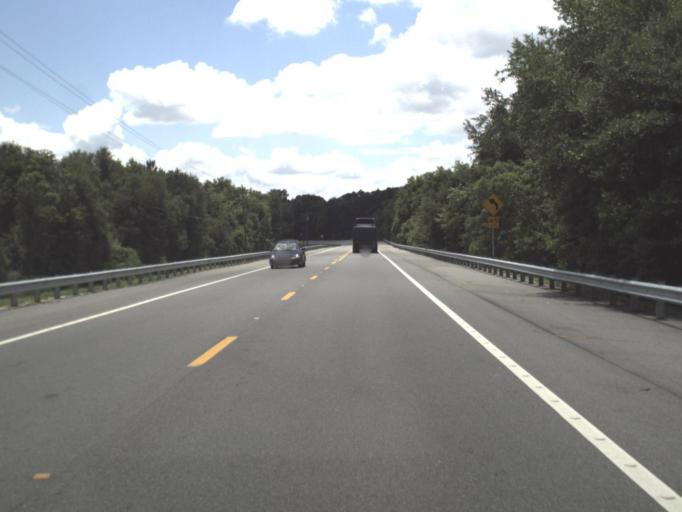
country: US
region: Florida
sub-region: Clay County
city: Keystone Heights
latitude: 29.7511
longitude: -81.9949
